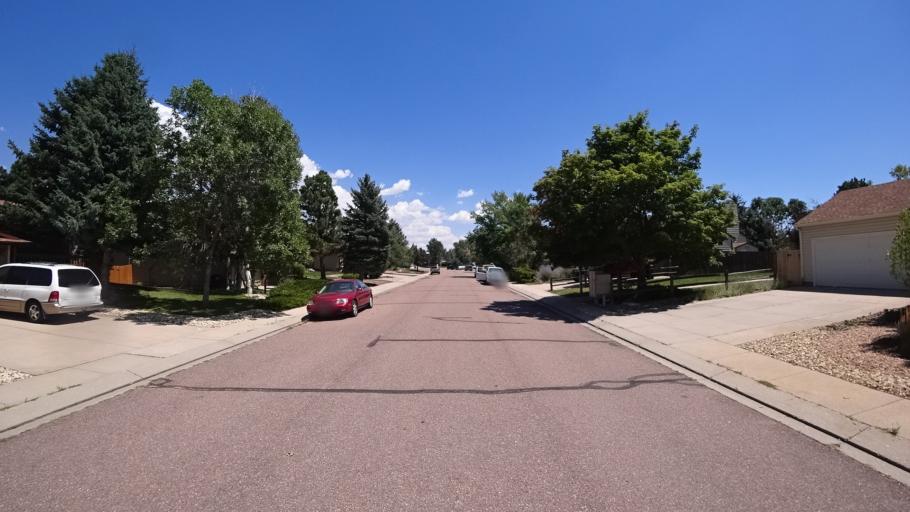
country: US
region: Colorado
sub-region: El Paso County
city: Black Forest
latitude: 38.9526
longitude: -104.7536
